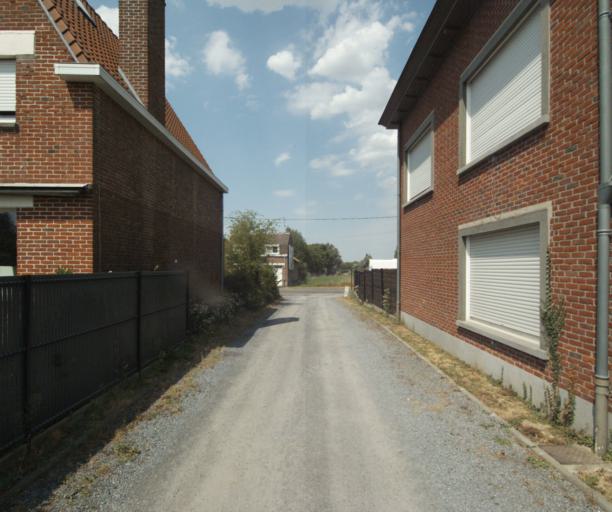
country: FR
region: Nord-Pas-de-Calais
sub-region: Departement du Nord
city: Comines
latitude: 50.7660
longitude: 3.0263
